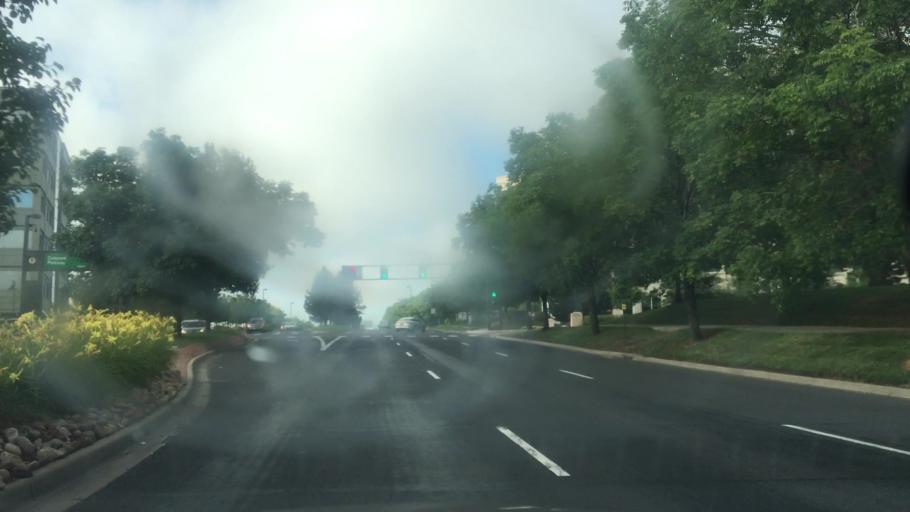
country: US
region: Colorado
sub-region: Arapahoe County
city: Castlewood
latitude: 39.6234
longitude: -104.8899
